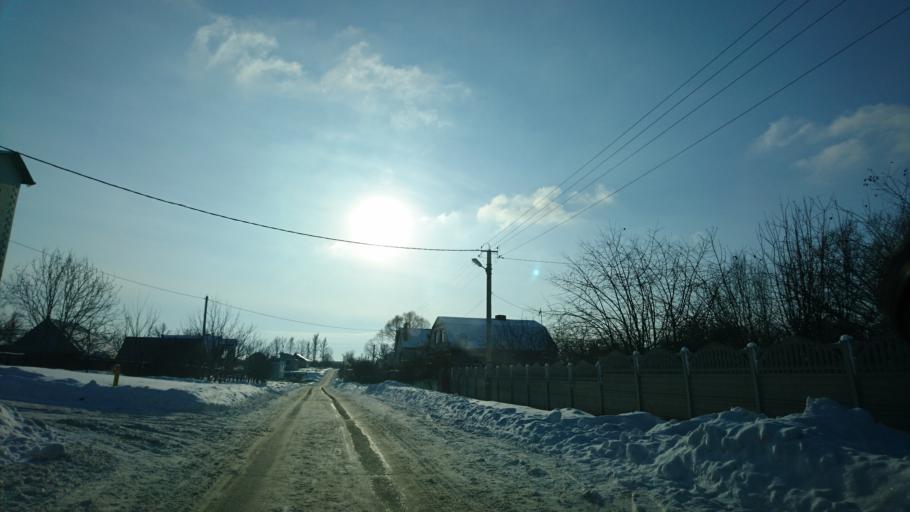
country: RU
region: Belgorod
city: Severnyy
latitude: 50.7234
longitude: 36.6107
